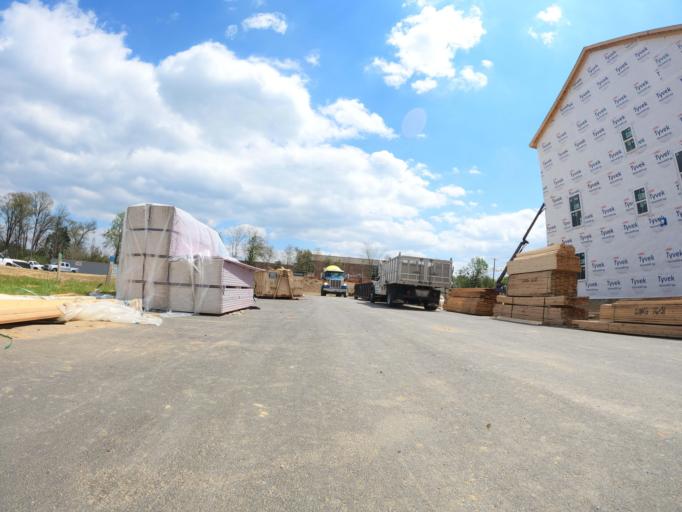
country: US
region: Maryland
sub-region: Howard County
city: Ellicott City
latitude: 39.2549
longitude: -76.8156
